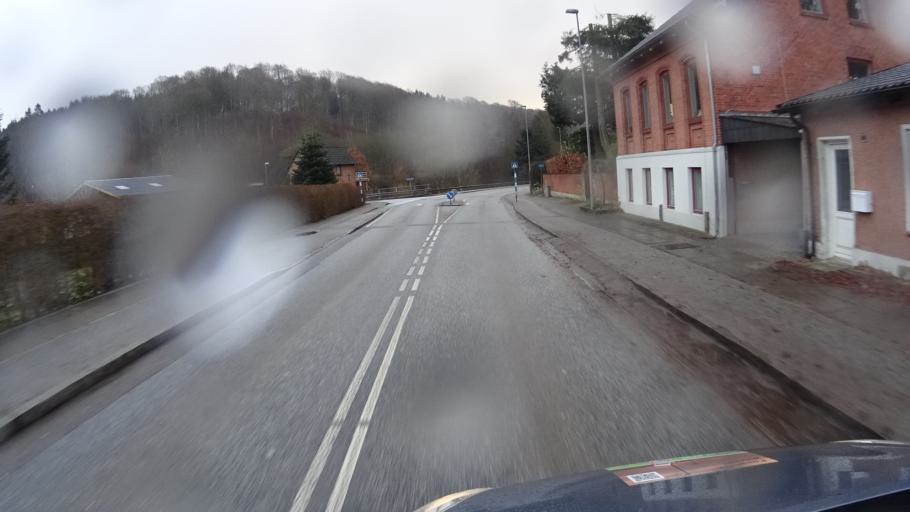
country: DK
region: South Denmark
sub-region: Vejle Kommune
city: Vejle
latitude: 55.7448
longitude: 9.5374
